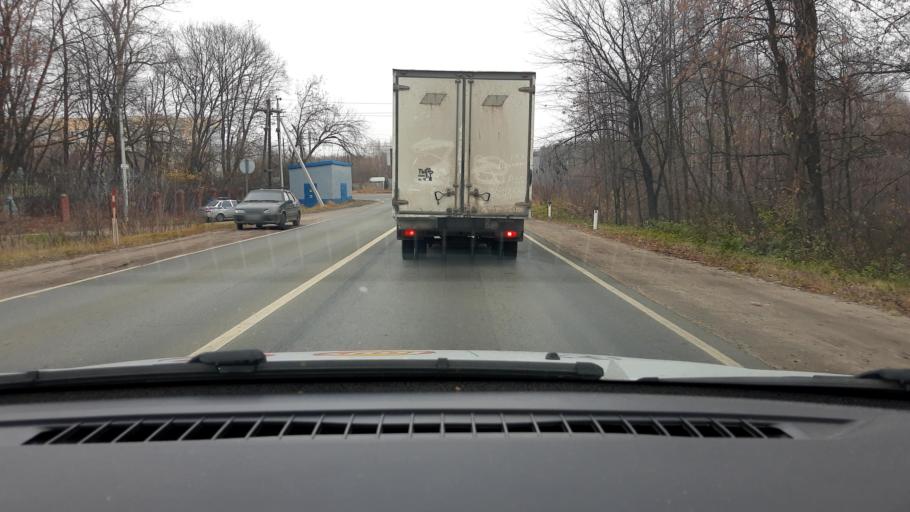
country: RU
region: Nizjnij Novgorod
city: Novaya Balakhna
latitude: 56.5164
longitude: 43.5809
